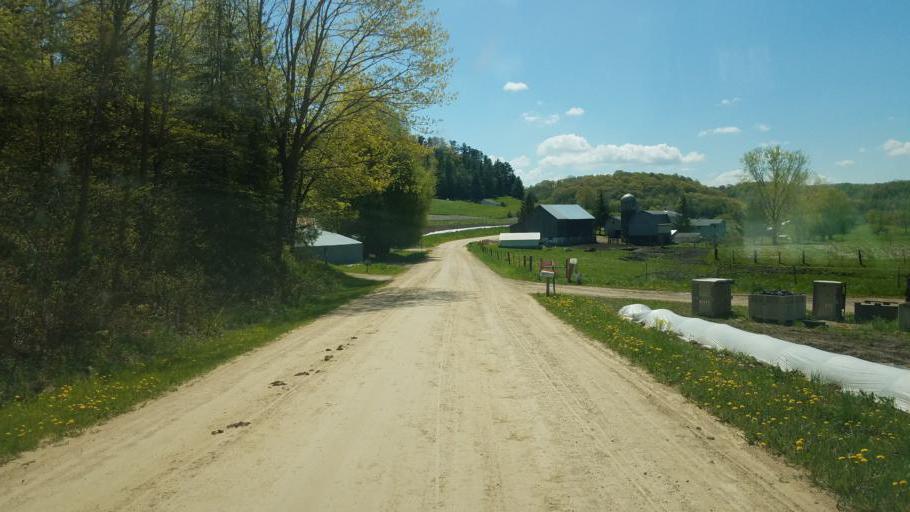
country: US
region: Wisconsin
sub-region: Vernon County
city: Hillsboro
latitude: 43.5903
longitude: -90.4088
